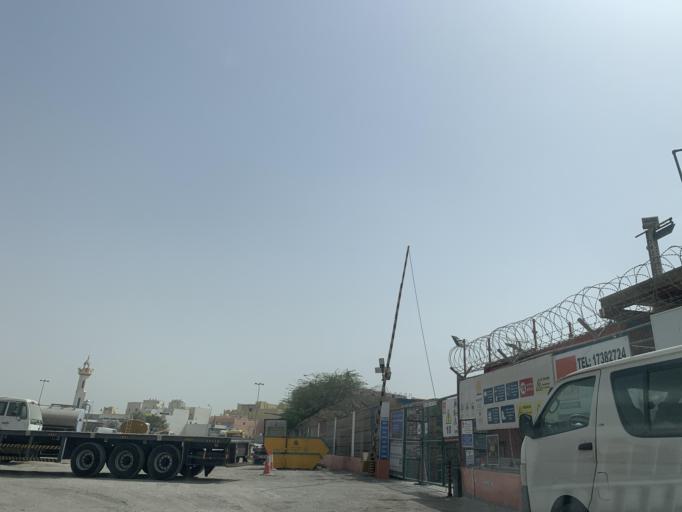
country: BH
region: Northern
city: Madinat `Isa
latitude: 26.1868
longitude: 50.5261
